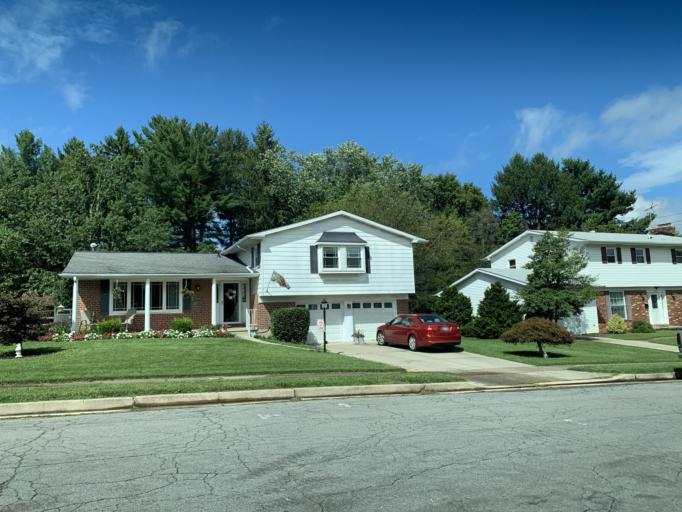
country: US
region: Maryland
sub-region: Baltimore County
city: Timonium
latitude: 39.4542
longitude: -76.6172
